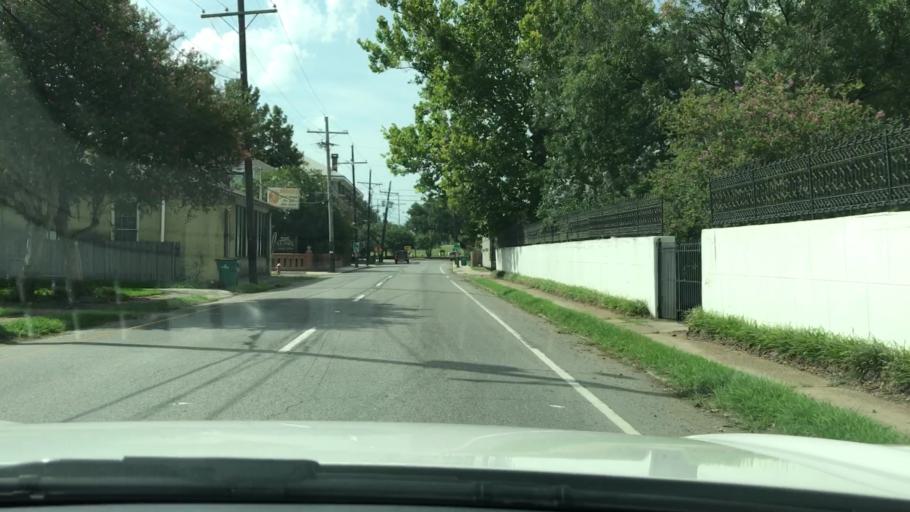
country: US
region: Louisiana
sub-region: Iberville Parish
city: Plaquemine
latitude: 30.2902
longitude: -91.2335
